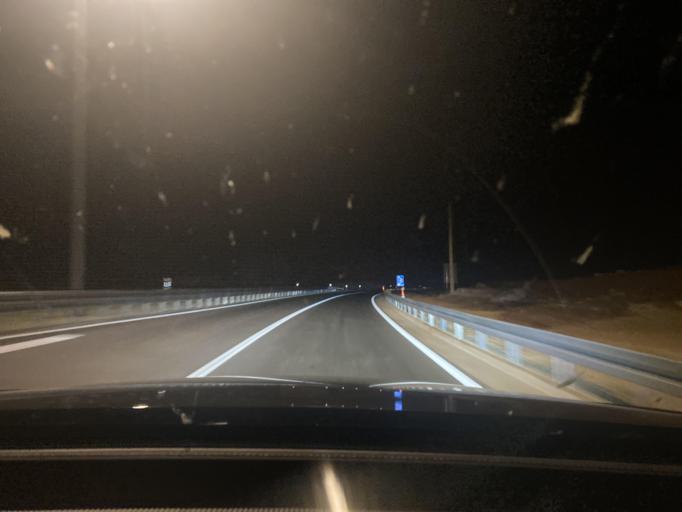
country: BA
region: Federation of Bosnia and Herzegovina
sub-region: Hercegovacko-Bosanski Kanton
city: Neum
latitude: 42.9179
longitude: 17.5276
